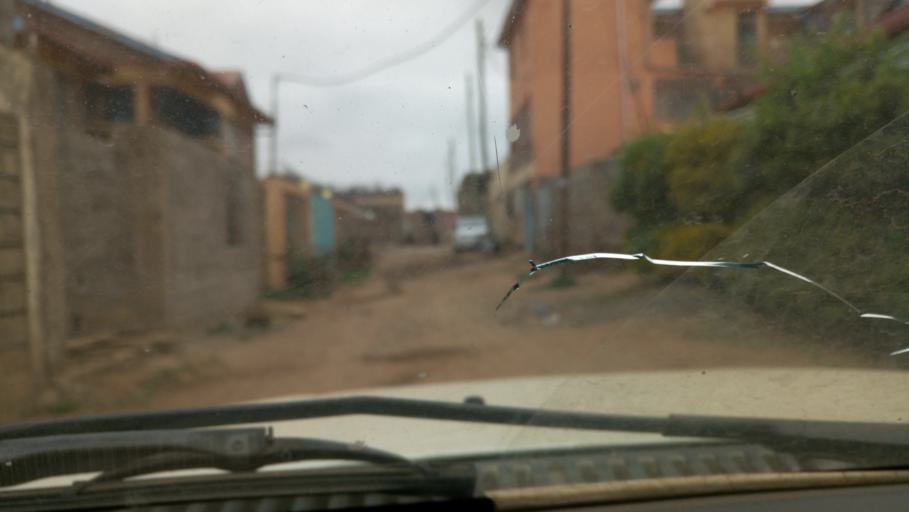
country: KE
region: Nairobi Area
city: Pumwani
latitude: -1.2502
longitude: 36.9278
